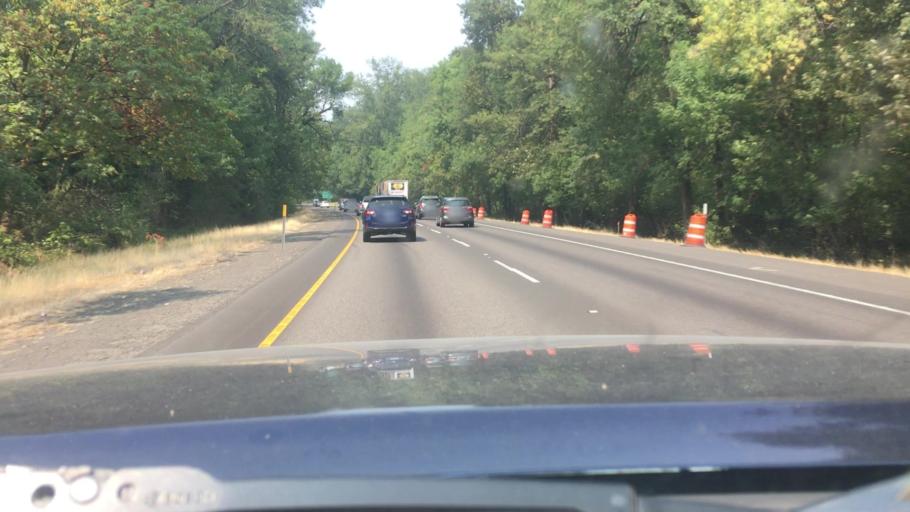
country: US
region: Oregon
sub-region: Clackamas County
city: Stafford
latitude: 45.3659
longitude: -122.6784
